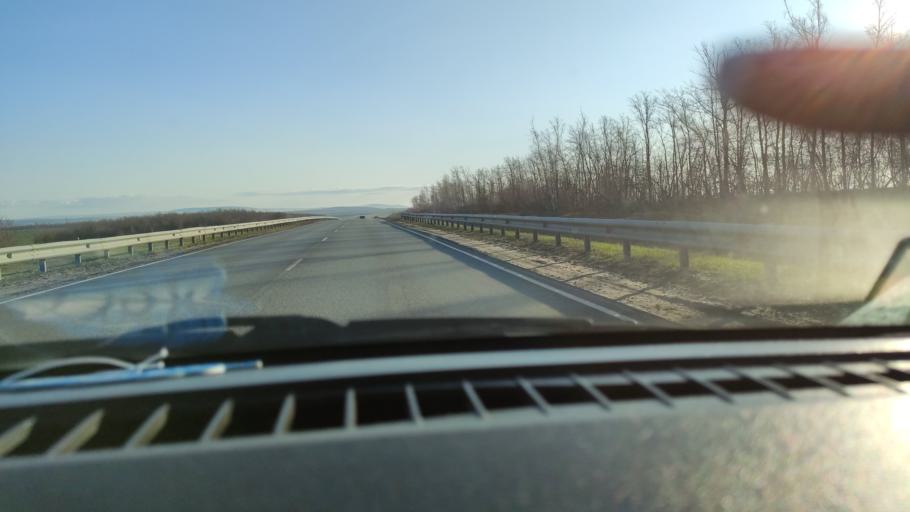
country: RU
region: Saratov
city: Balakovo
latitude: 52.1006
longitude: 47.7350
